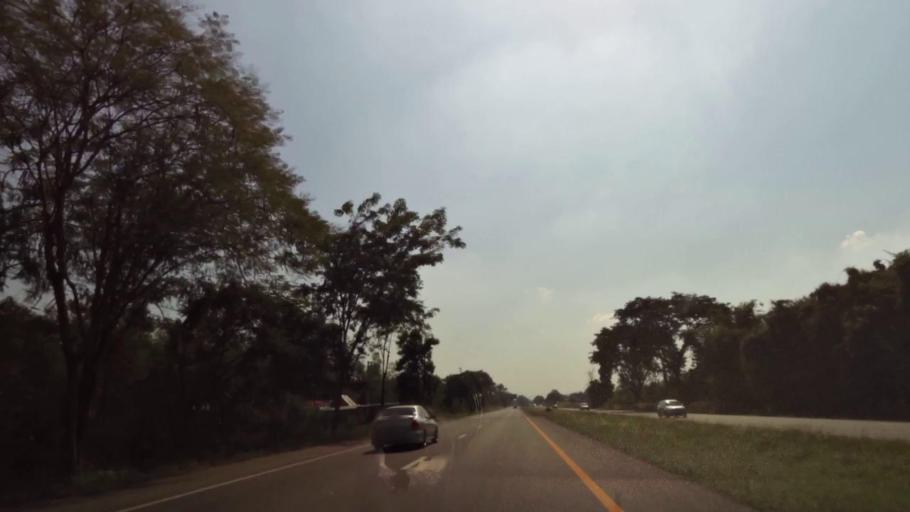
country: TH
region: Phichit
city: Bueng Na Rang
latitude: 16.1989
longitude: 100.1281
